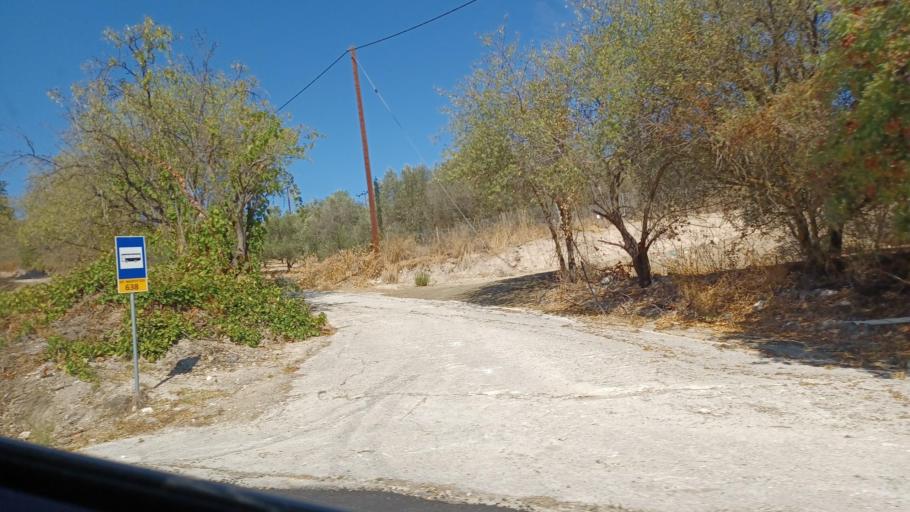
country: CY
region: Pafos
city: Mesogi
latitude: 34.9245
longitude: 32.5674
